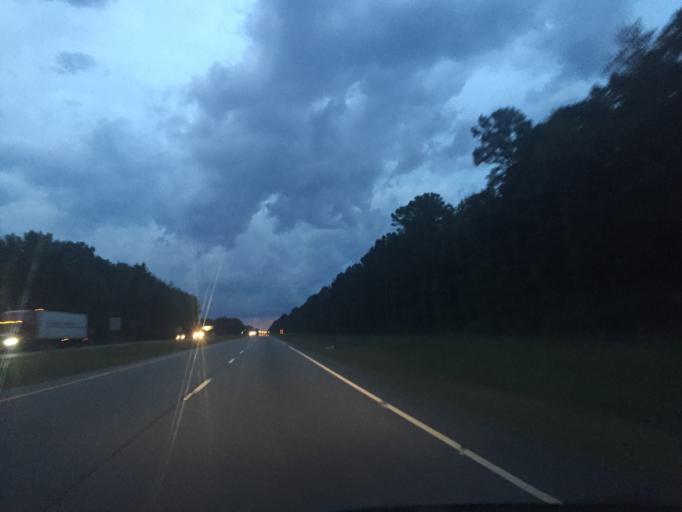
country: US
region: Georgia
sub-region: Bryan County
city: Richmond Hill
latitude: 31.9024
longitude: -81.3658
